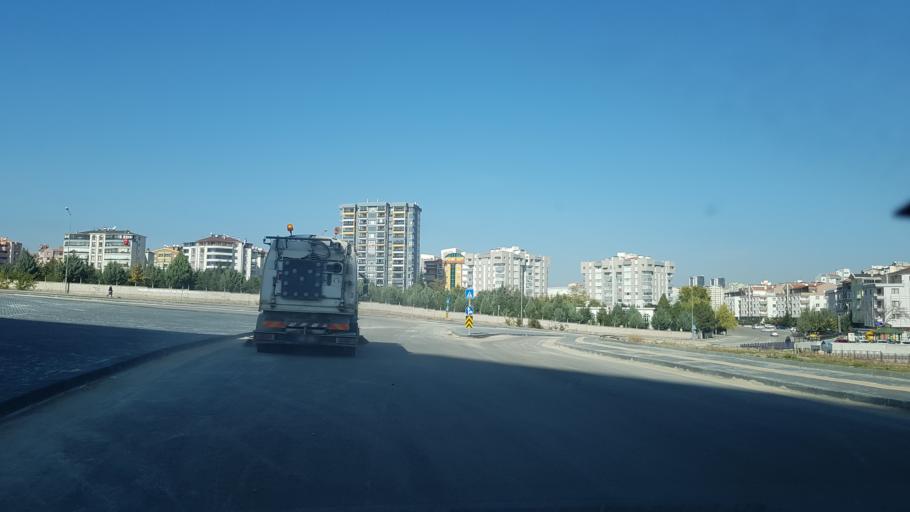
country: TR
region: Ankara
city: Etimesgut
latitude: 39.9725
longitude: 32.6122
